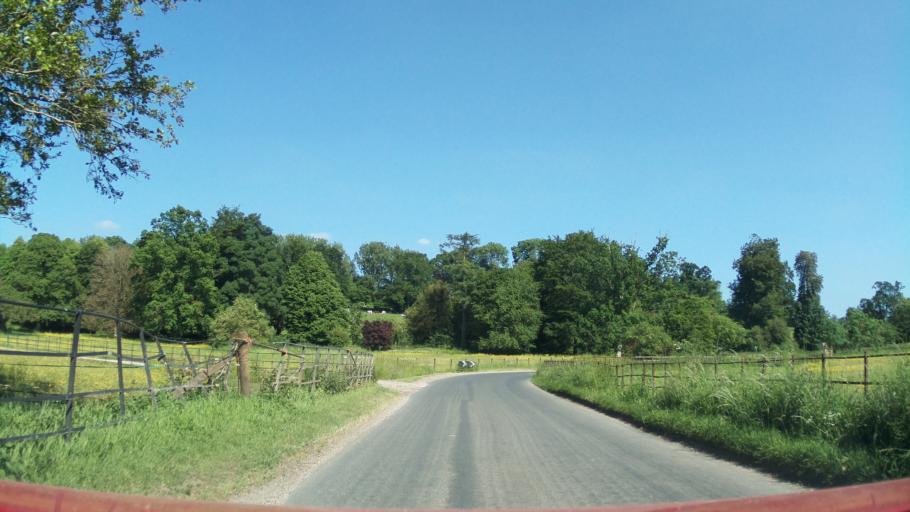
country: GB
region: England
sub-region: Hampshire
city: Abbotts Ann
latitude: 51.2556
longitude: -1.5797
